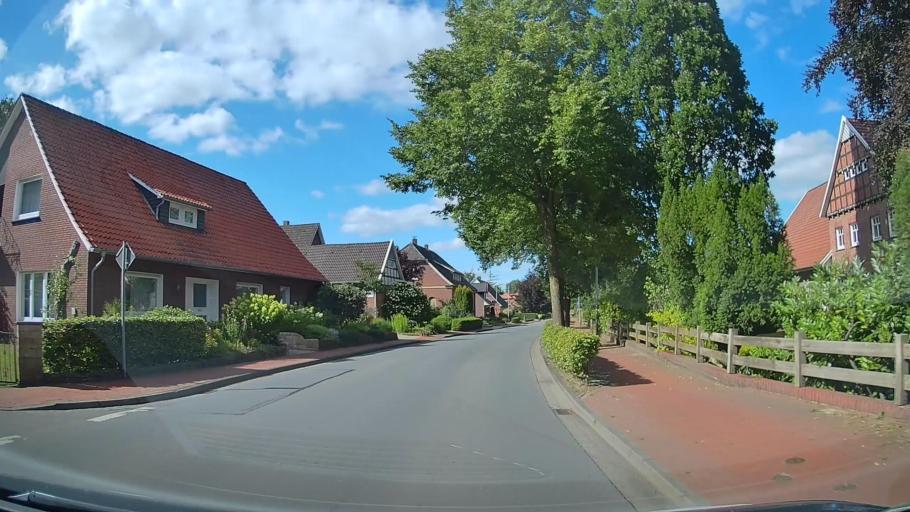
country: DE
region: Lower Saxony
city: Berge
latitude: 52.6158
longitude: 7.7468
